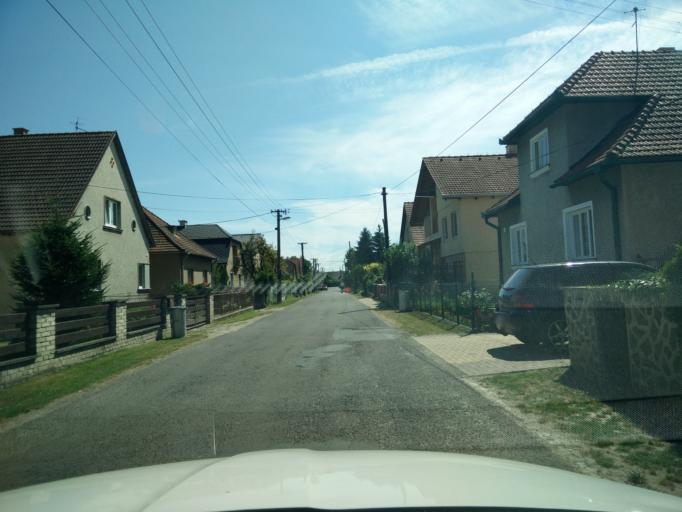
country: SK
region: Nitriansky
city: Prievidza
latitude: 48.8562
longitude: 18.6489
